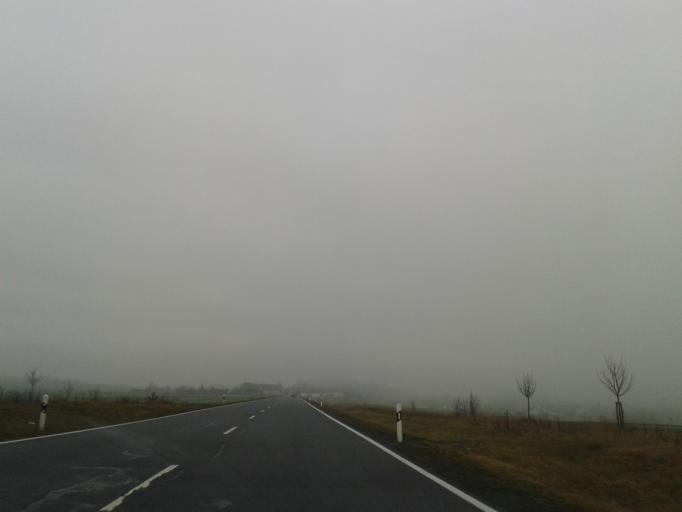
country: DE
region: Bavaria
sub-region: Regierungsbezirk Unterfranken
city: Pfarrweisach
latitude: 50.1926
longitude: 10.7486
